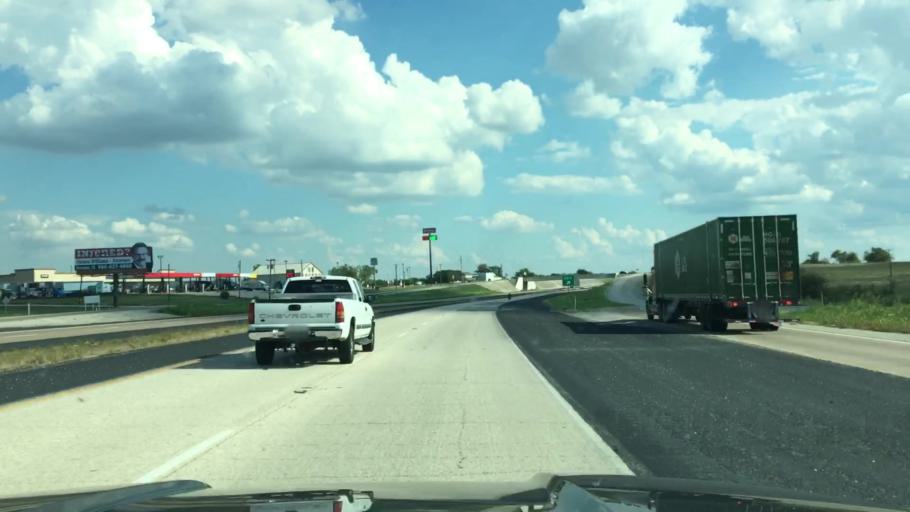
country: US
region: Texas
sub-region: Wise County
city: New Fairview
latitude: 33.1044
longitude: -97.4728
